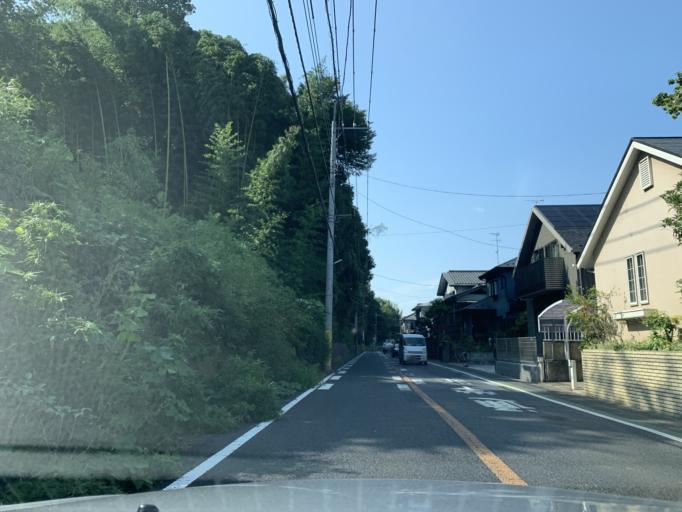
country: JP
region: Chiba
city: Kashiwa
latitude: 35.8440
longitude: 139.9357
